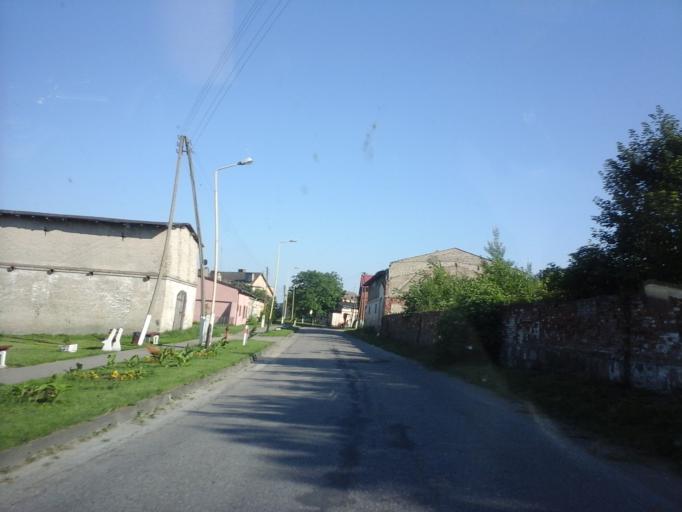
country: PL
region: West Pomeranian Voivodeship
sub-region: Powiat lobeski
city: Dobra
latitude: 53.5309
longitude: 15.3137
